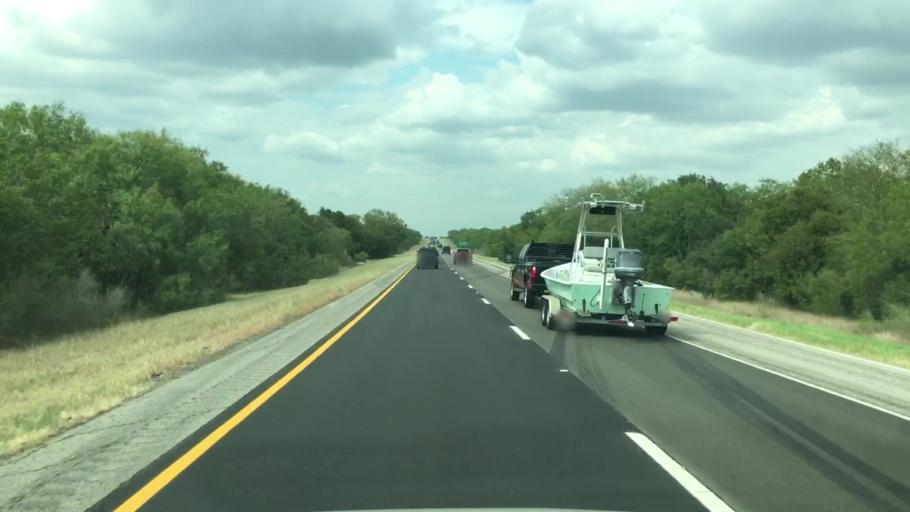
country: US
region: Texas
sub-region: Atascosa County
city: Pleasanton
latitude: 28.9295
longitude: -98.4351
